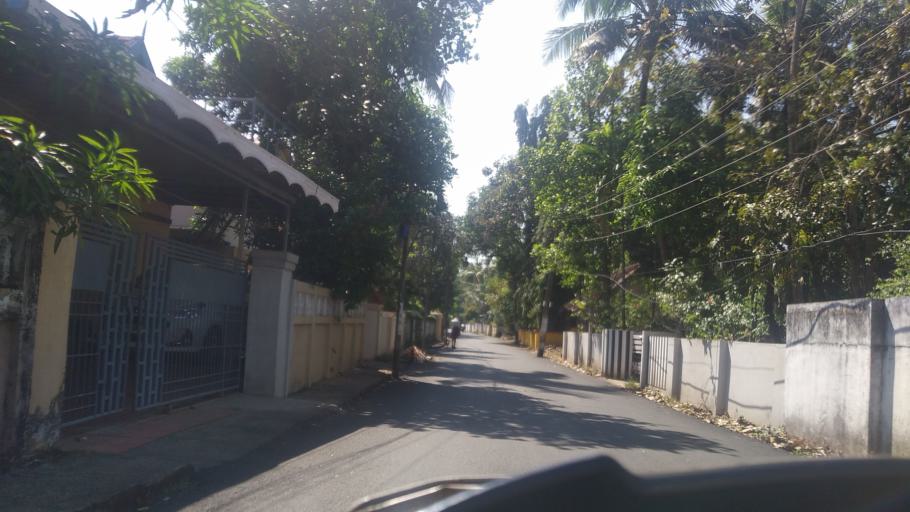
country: IN
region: Kerala
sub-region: Ernakulam
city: Elur
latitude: 10.0417
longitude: 76.2231
